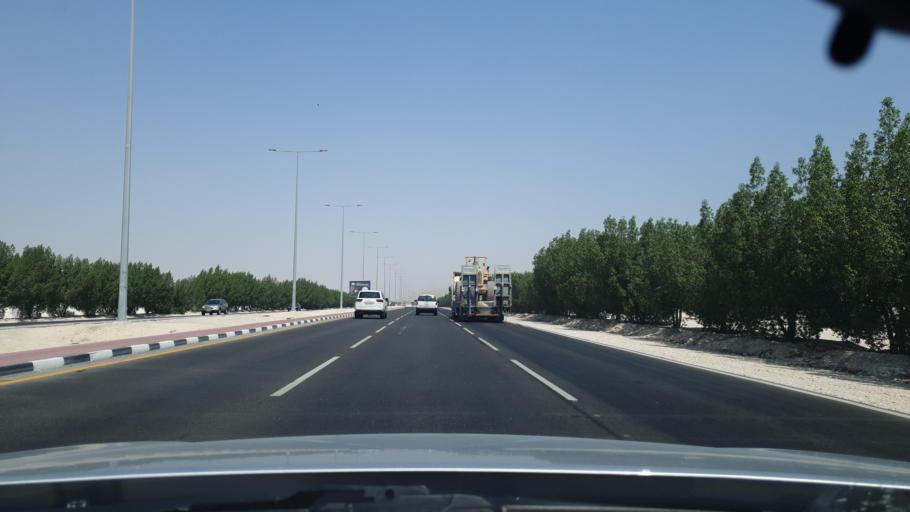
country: QA
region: Al Khawr
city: Al Khawr
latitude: 25.7003
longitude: 51.5032
